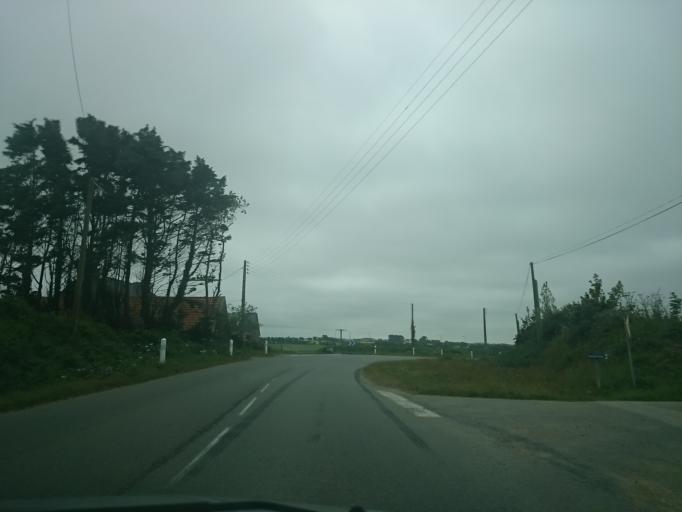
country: FR
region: Brittany
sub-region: Departement du Finistere
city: Landeda
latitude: 48.5538
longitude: -4.5566
